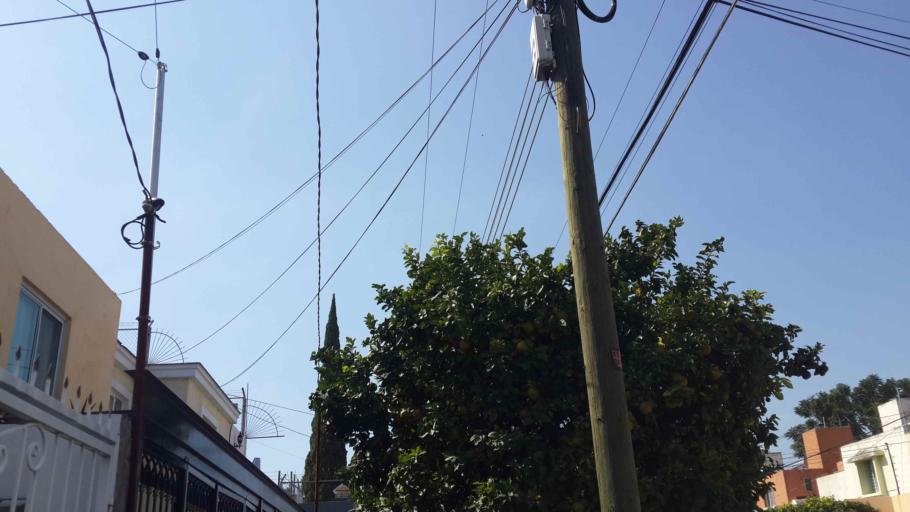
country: MX
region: Jalisco
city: Guadalajara
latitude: 20.6680
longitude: -103.4302
